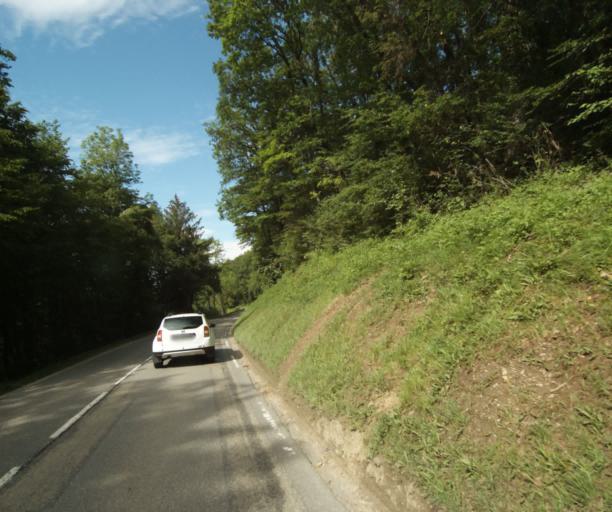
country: FR
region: Rhone-Alpes
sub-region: Departement de la Haute-Savoie
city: Allinges
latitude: 46.3473
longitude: 6.4776
